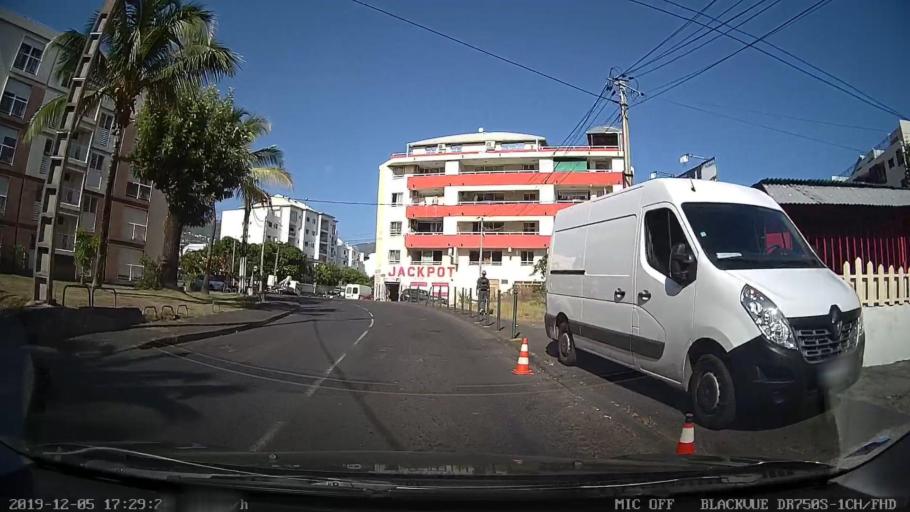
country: RE
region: Reunion
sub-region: Reunion
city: Saint-Denis
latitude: -20.8961
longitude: 55.4815
